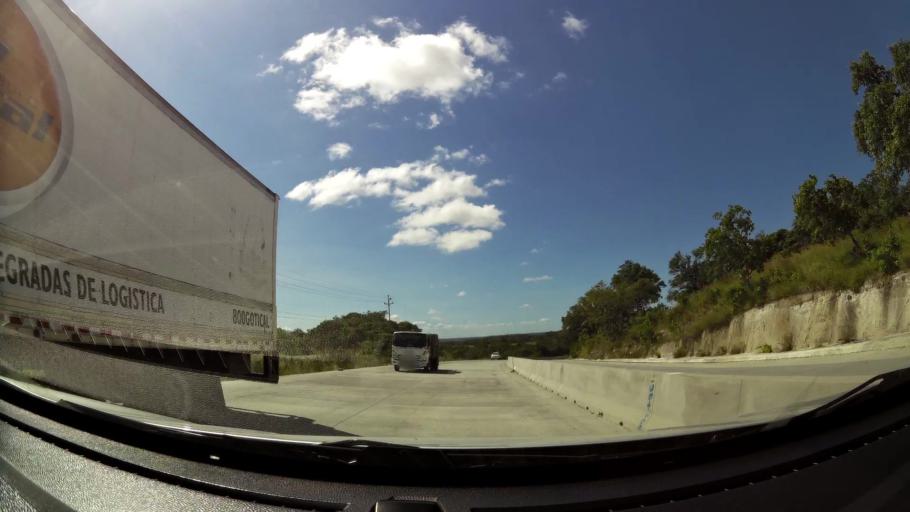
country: CR
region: Guanacaste
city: Bagaces
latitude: 10.5380
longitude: -85.3299
